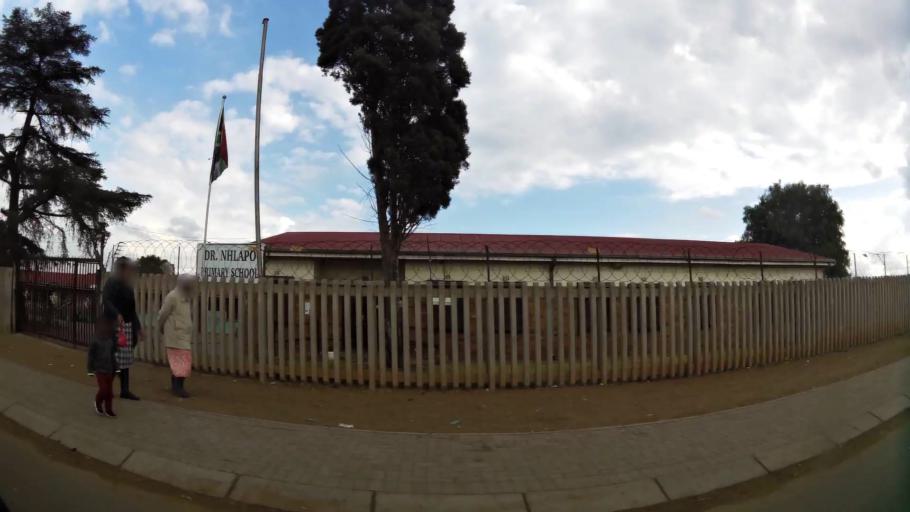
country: ZA
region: Gauteng
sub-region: Sedibeng District Municipality
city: Vanderbijlpark
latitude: -26.6679
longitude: 27.8489
